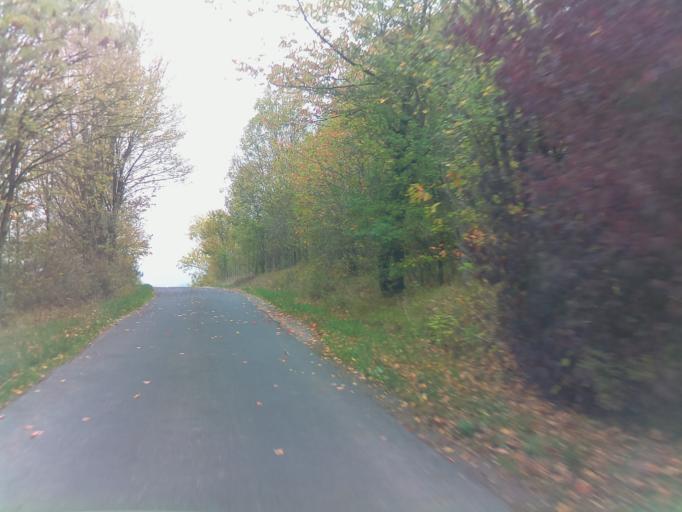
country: DE
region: Hesse
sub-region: Regierungsbezirk Kassel
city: Poppenhausen
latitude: 50.4958
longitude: 9.8576
